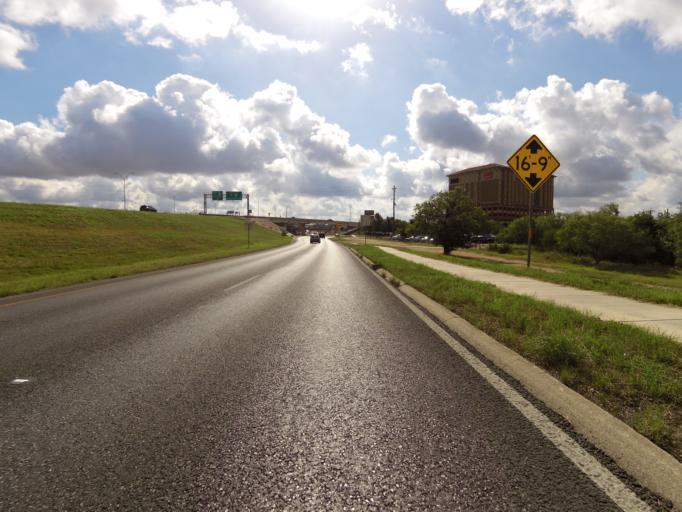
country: US
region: Texas
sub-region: Bexar County
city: Shavano Park
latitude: 29.5897
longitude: -98.6027
